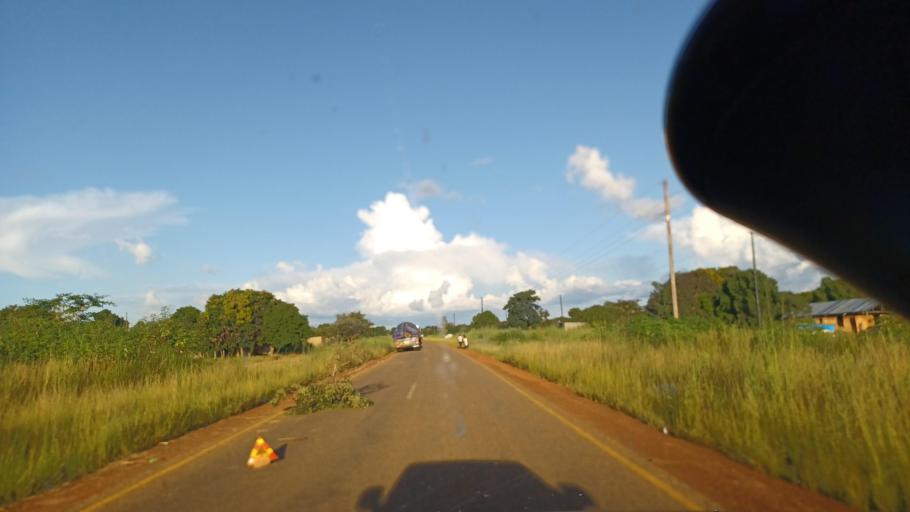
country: ZM
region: North-Western
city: Kalengwa
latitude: -13.1424
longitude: 25.0288
